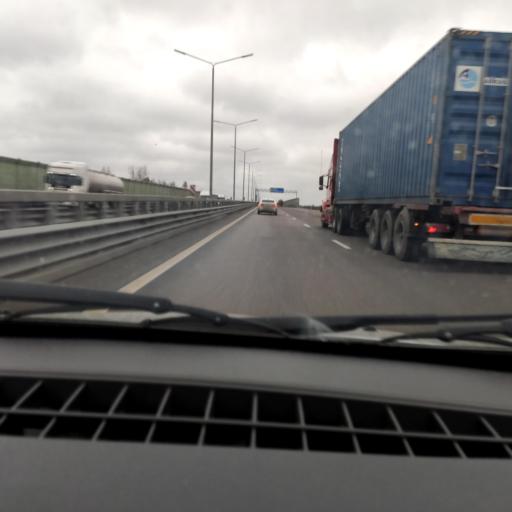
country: RU
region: Voronezj
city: Podgornoye
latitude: 51.8157
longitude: 39.2521
